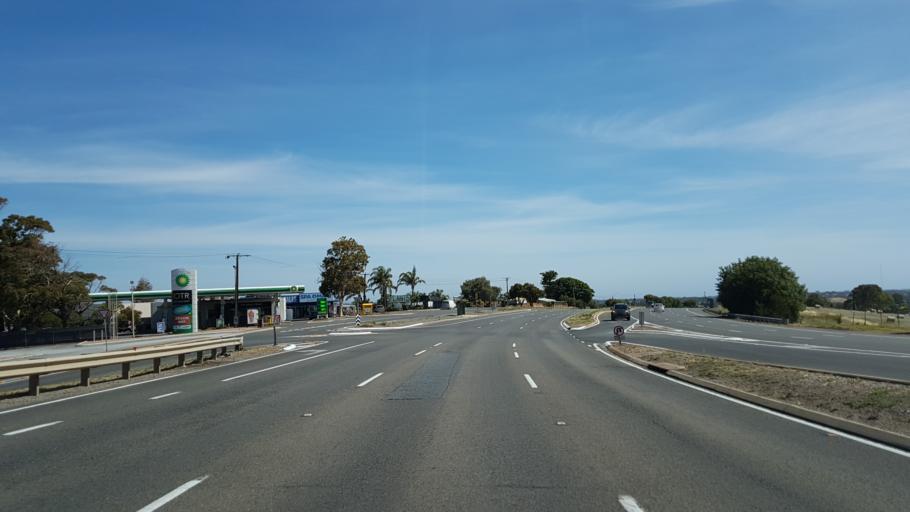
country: AU
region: South Australia
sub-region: Marion
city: Trott Park
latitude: -35.0700
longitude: 138.5544
